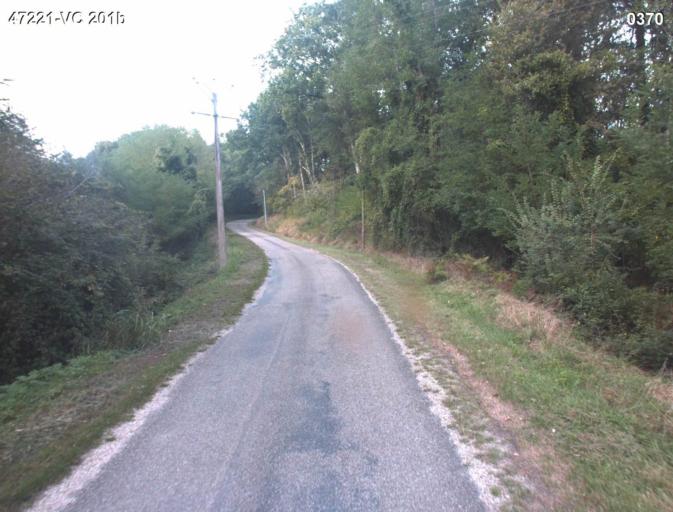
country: FR
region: Aquitaine
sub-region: Departement du Lot-et-Garonne
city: Mezin
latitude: 44.0776
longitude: 0.2431
